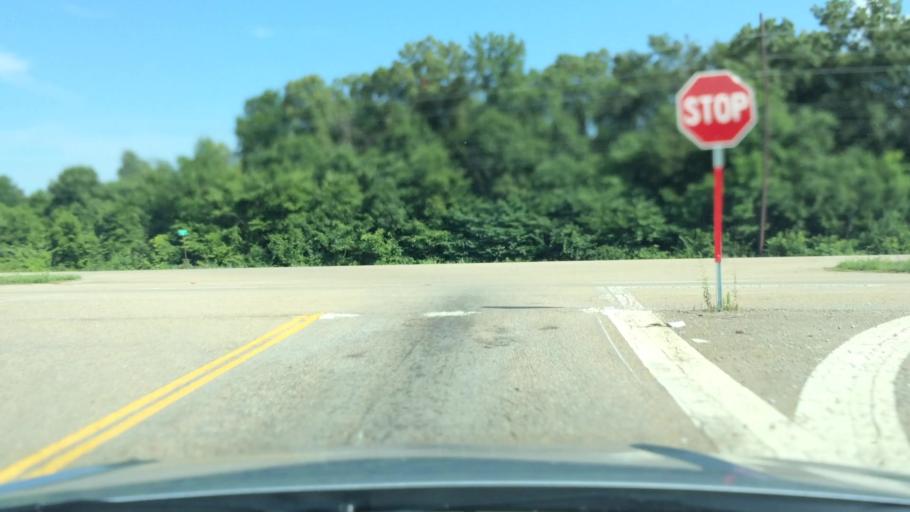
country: US
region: Tennessee
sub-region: Hamblen County
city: Morristown
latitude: 36.1660
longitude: -83.3667
